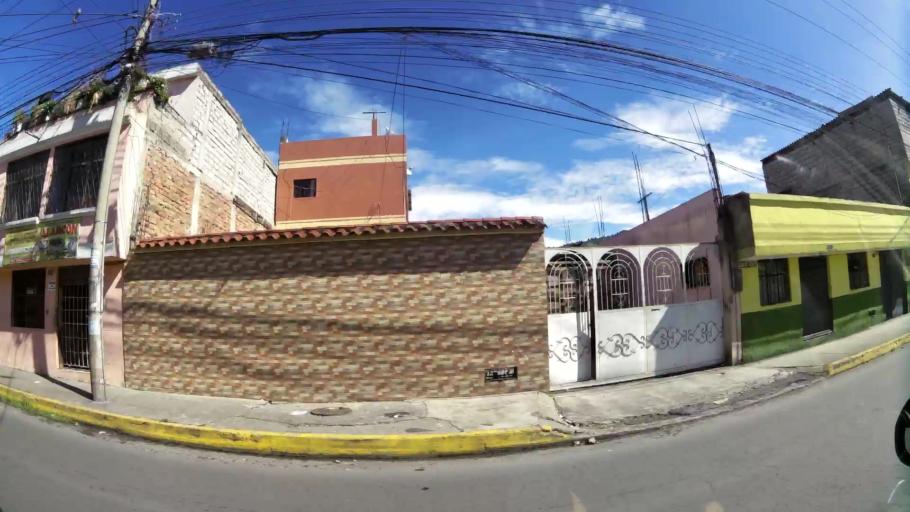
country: EC
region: Pichincha
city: Quito
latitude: -0.2821
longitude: -78.5579
